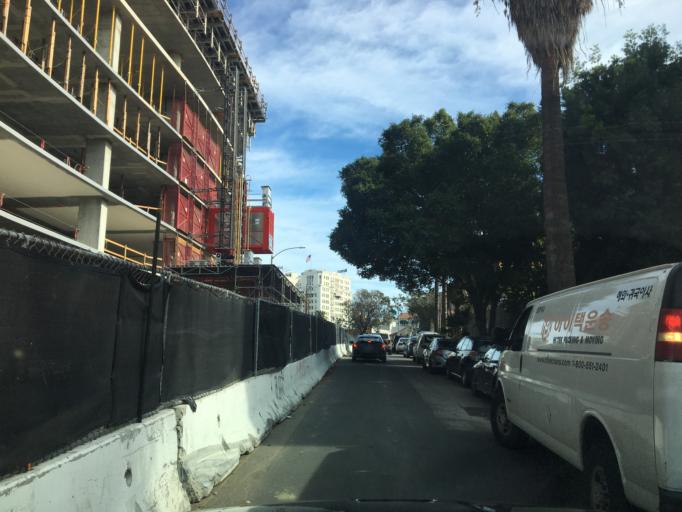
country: US
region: California
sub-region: Los Angeles County
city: Silver Lake
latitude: 34.0608
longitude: -118.2857
